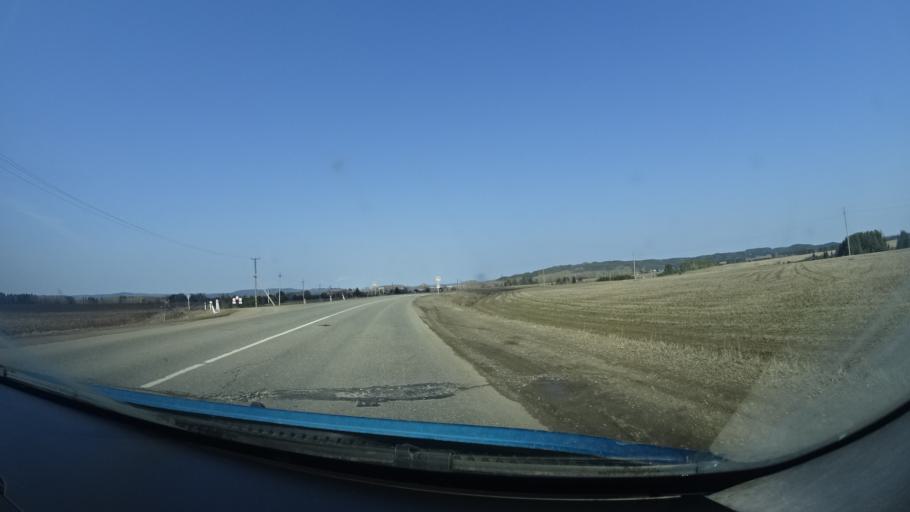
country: RU
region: Perm
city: Osa
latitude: 57.2804
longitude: 55.5661
